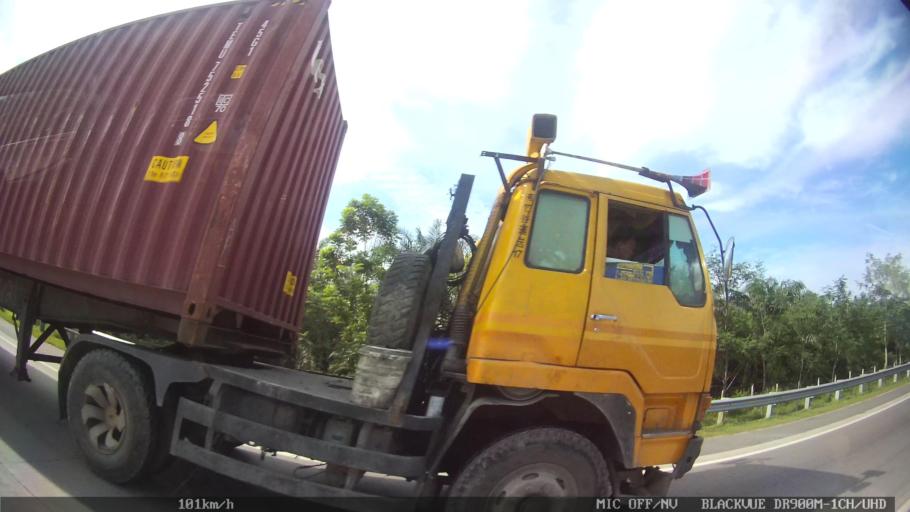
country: ID
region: North Sumatra
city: Sunggal
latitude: 3.6384
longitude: 98.6086
